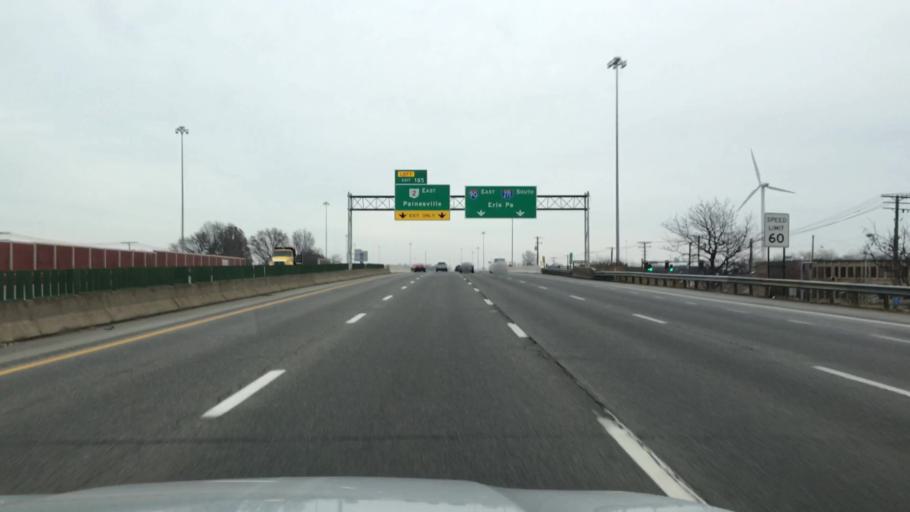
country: US
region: Ohio
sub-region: Cuyahoga County
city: Euclid
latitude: 41.6005
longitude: -81.5044
